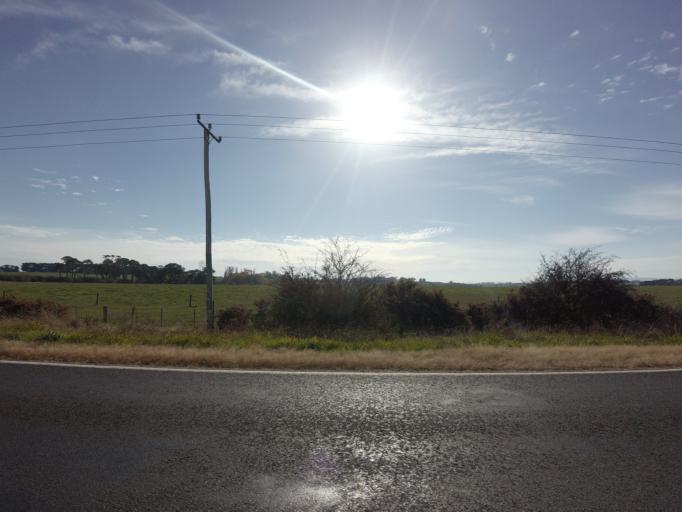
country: AU
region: Tasmania
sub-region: Meander Valley
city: Westbury
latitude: -41.5273
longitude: 146.9344
